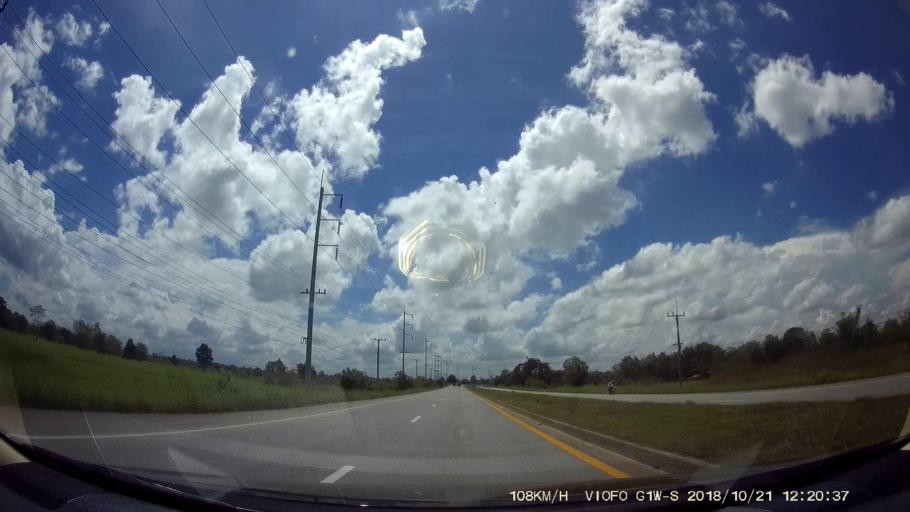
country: TH
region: Nakhon Ratchasima
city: Dan Khun Thot
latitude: 15.2854
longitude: 101.8013
